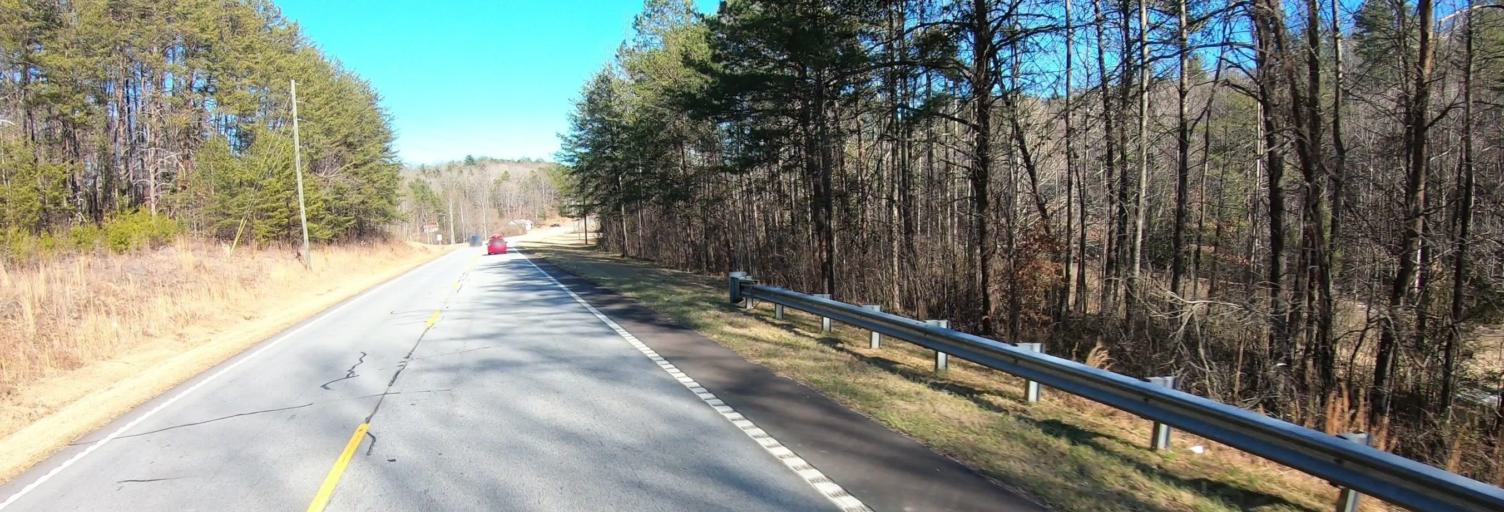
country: US
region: South Carolina
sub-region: Pickens County
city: Pickens
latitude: 34.9747
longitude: -82.8027
